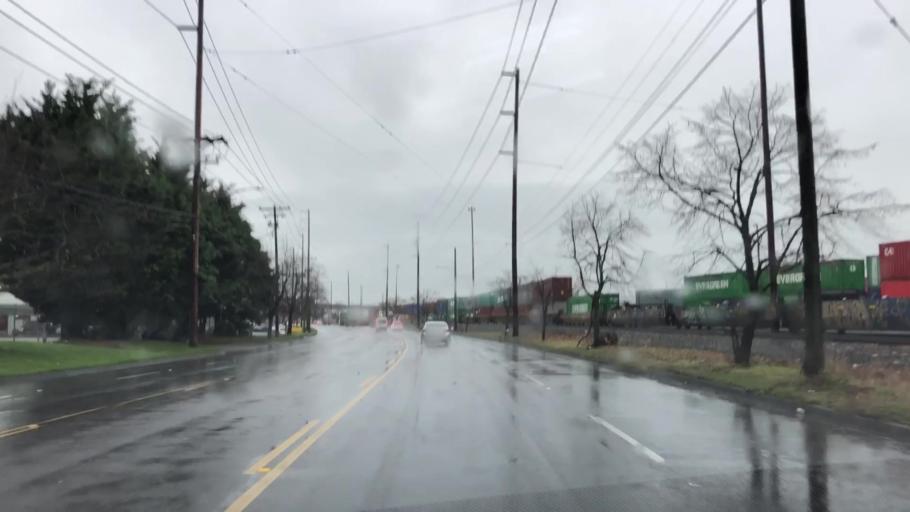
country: US
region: Washington
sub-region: Pierce County
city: Tacoma
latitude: 47.2511
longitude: -122.4014
